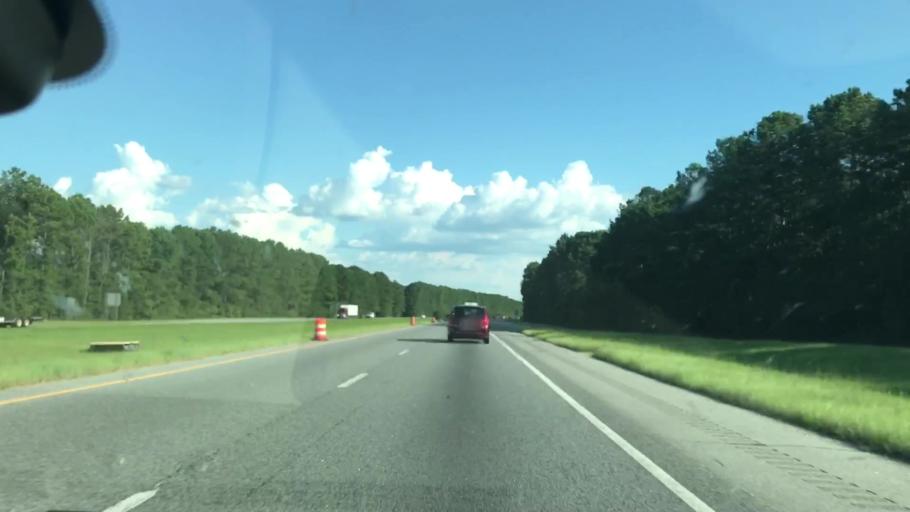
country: US
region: Georgia
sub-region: Harris County
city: Hamilton
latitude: 32.6600
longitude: -84.9787
